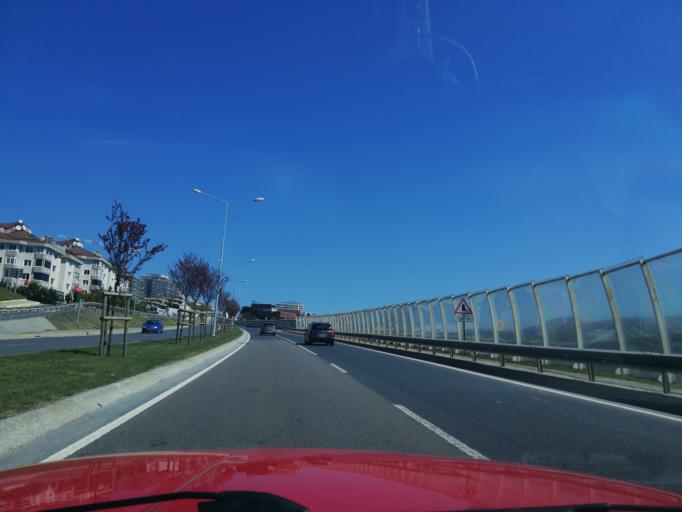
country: TR
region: Istanbul
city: Umraniye
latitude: 41.1066
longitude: 29.1072
